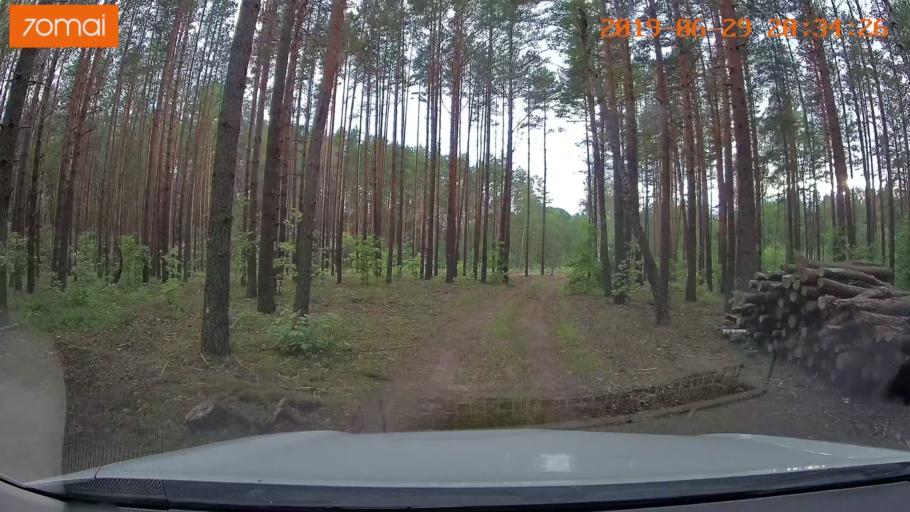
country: BY
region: Brest
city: Hantsavichy
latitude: 52.5141
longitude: 26.3465
